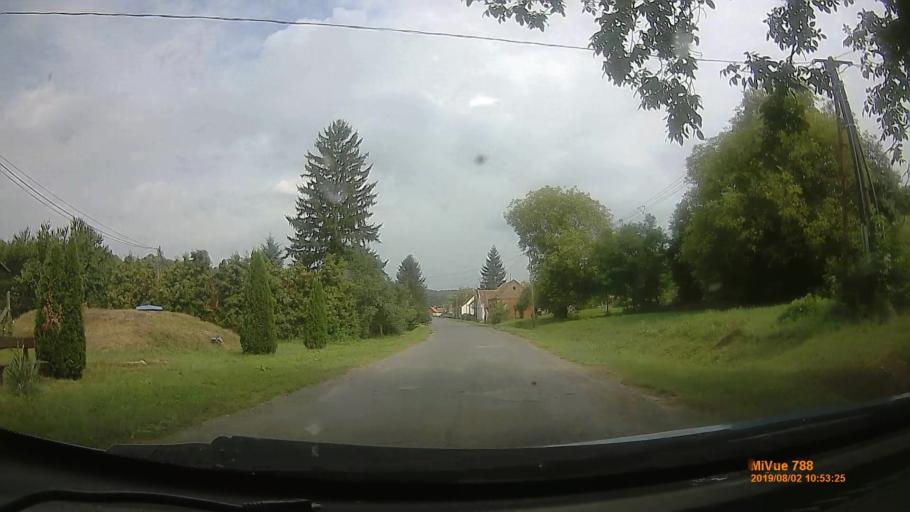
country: HU
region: Baranya
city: Buekkoesd
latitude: 46.0953
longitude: 17.9571
